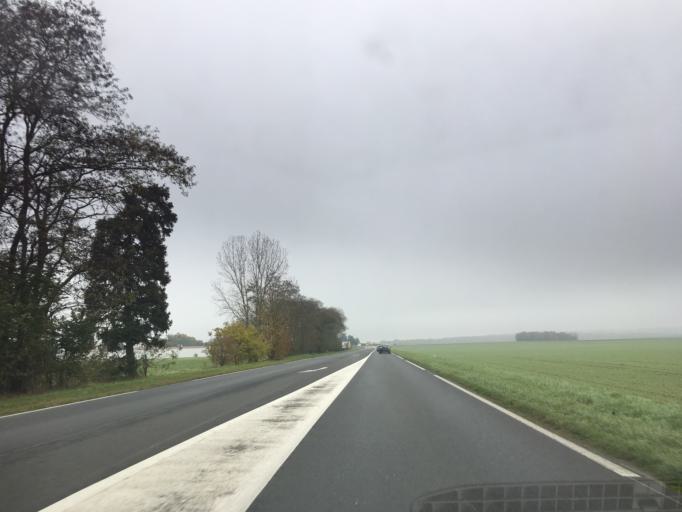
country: FR
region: Ile-de-France
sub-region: Departement de Seine-et-Marne
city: Cannes-Ecluse
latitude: 48.3593
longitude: 2.9761
